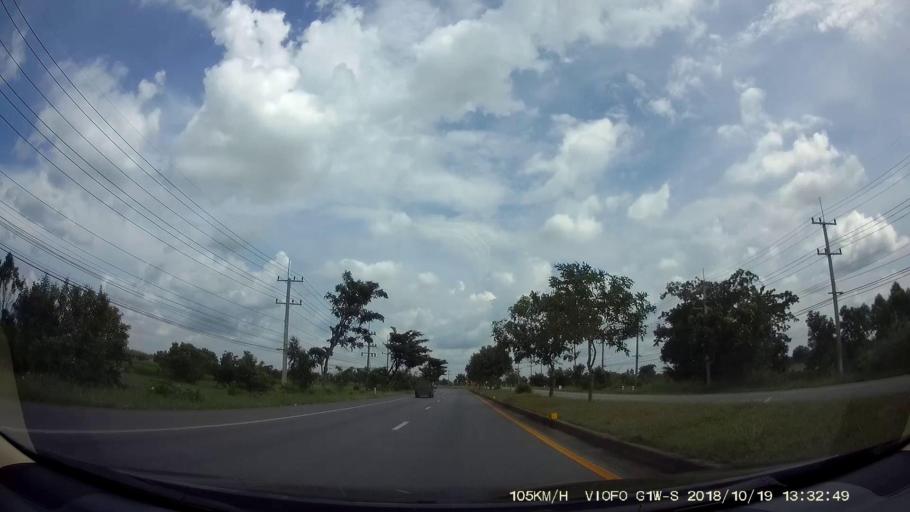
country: TH
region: Chaiyaphum
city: Chatturat
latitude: 15.5769
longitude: 101.8878
